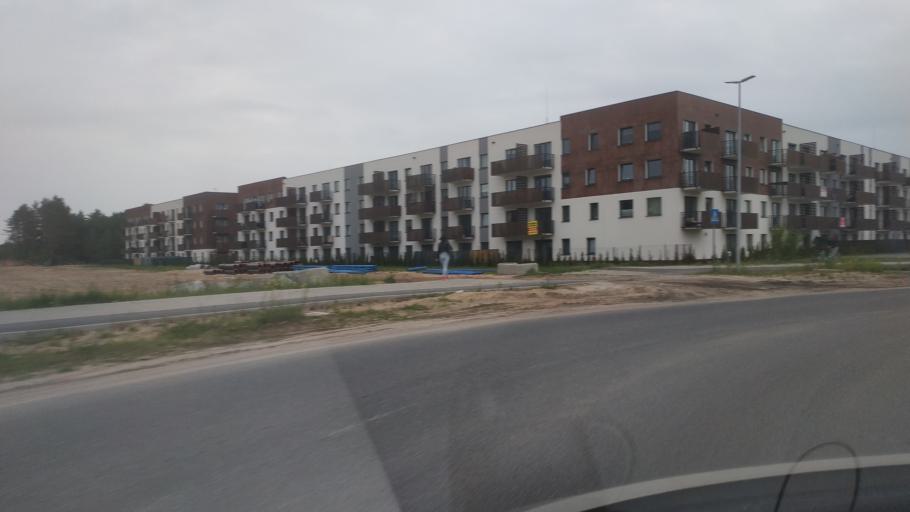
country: PL
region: Kujawsko-Pomorskie
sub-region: Powiat torunski
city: Lysomice
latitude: 53.0527
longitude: 18.6034
